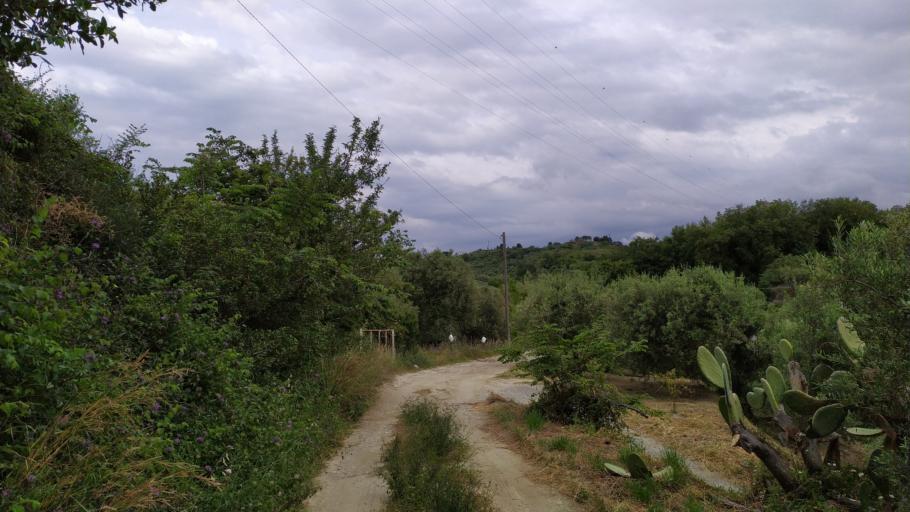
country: IT
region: Sicily
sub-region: Messina
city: Gualtieri Sicamino
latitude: 38.1580
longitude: 15.2974
